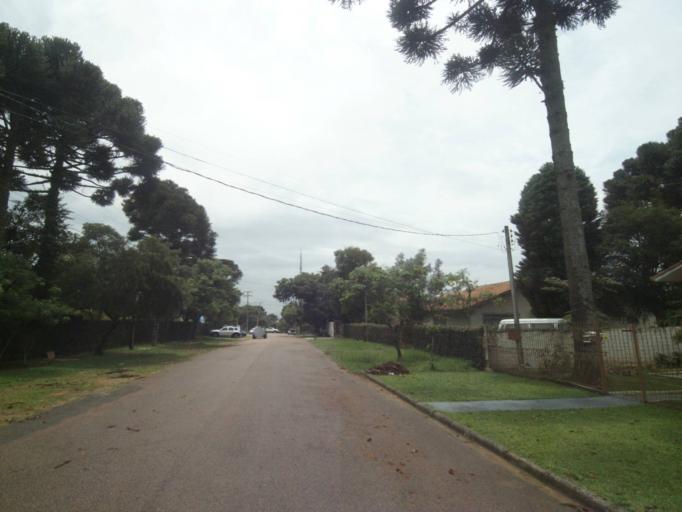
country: BR
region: Parana
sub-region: Curitiba
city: Curitiba
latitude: -25.4161
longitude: -49.2914
